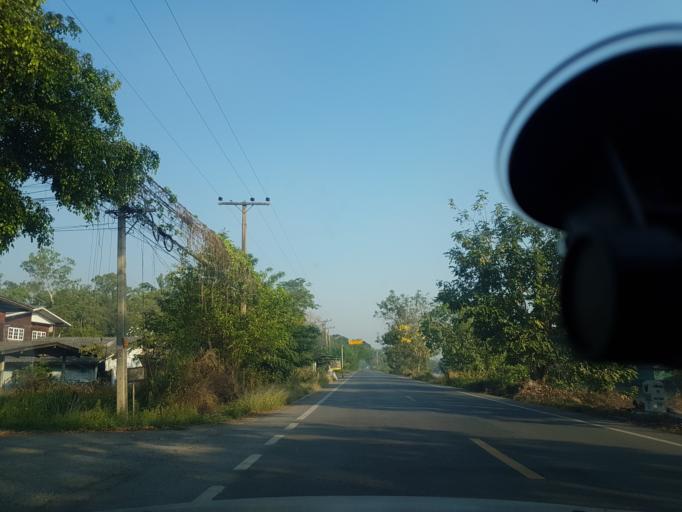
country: TH
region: Pathum Thani
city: Nong Suea
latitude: 14.0957
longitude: 100.8685
